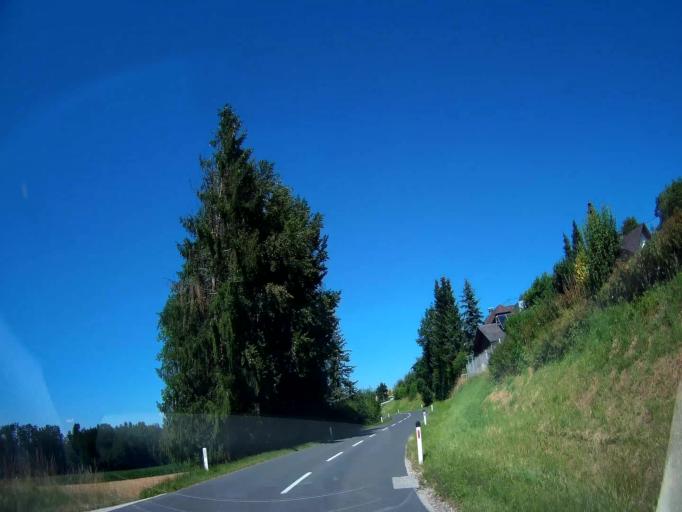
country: AT
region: Carinthia
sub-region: Politischer Bezirk Volkermarkt
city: Gallizien
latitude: 46.6079
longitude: 14.5370
